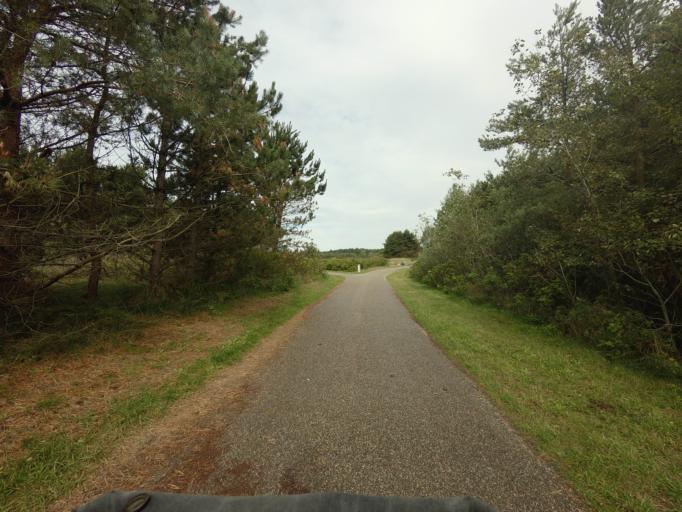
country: NL
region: Friesland
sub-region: Gemeente Ameland
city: Nes
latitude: 53.4491
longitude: 5.7813
